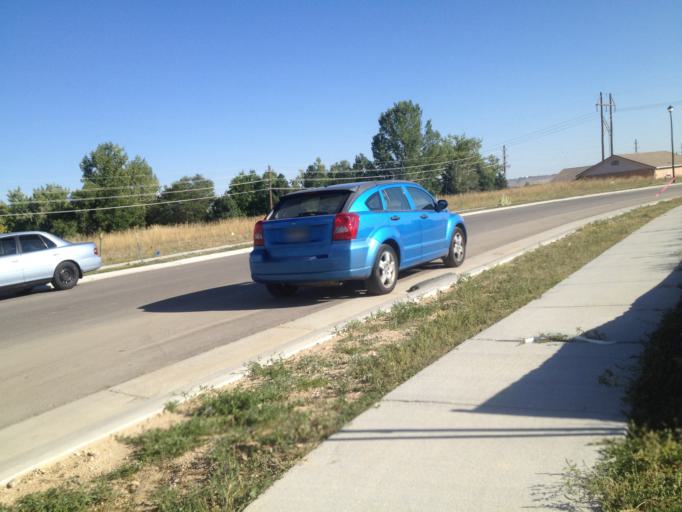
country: US
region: Colorado
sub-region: Boulder County
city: Louisville
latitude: 39.9918
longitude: -105.1194
